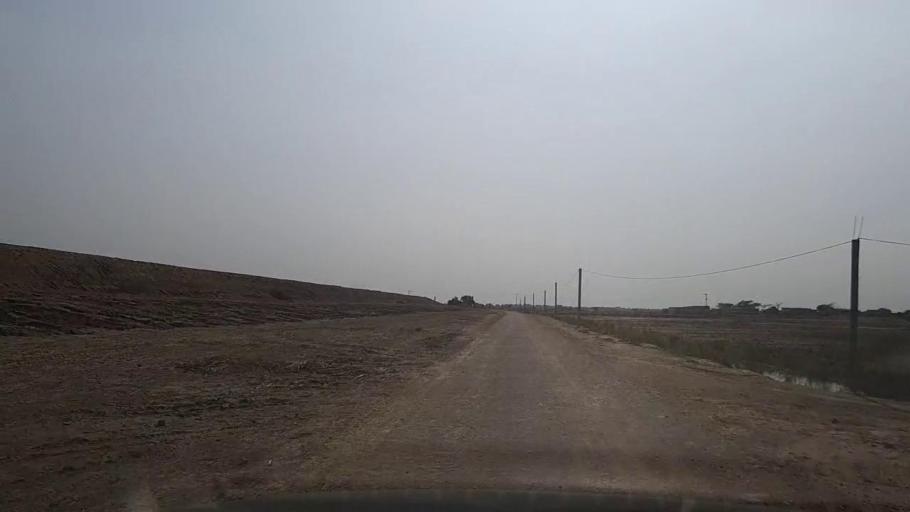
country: PK
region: Sindh
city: Thatta
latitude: 24.5656
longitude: 67.9132
